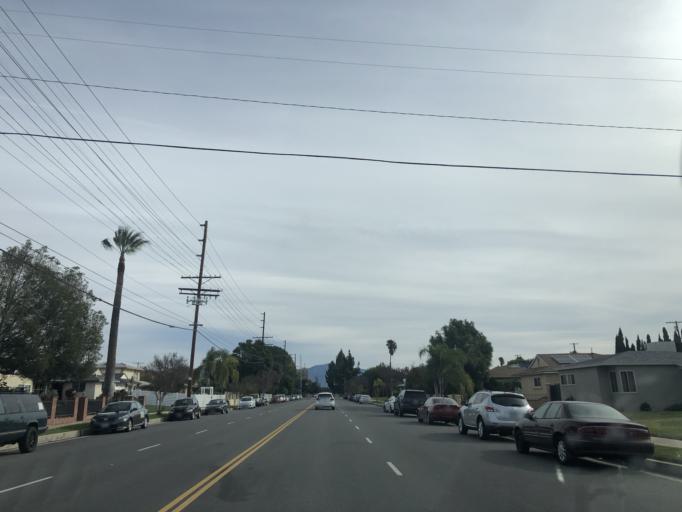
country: US
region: California
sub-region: Los Angeles County
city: San Fernando
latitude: 34.2720
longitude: -118.4831
